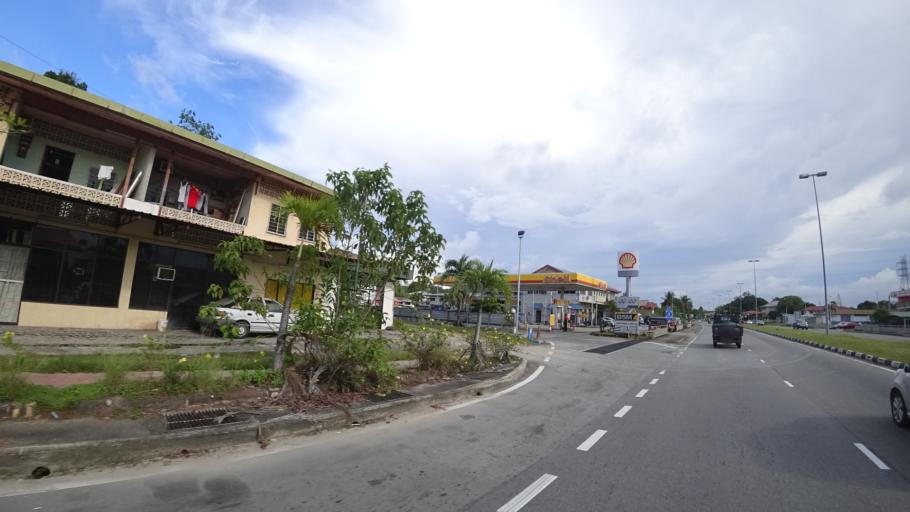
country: BN
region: Brunei and Muara
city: Bandar Seri Begawan
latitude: 4.8763
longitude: 114.8605
